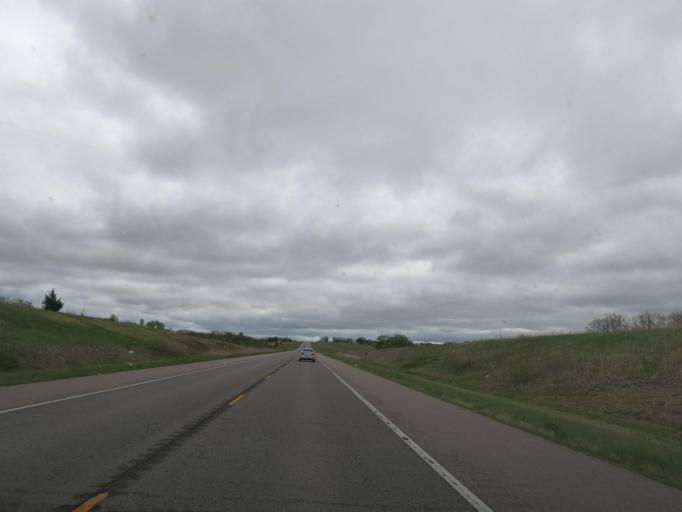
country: US
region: Kansas
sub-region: Elk County
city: Howard
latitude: 37.6363
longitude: -96.3306
